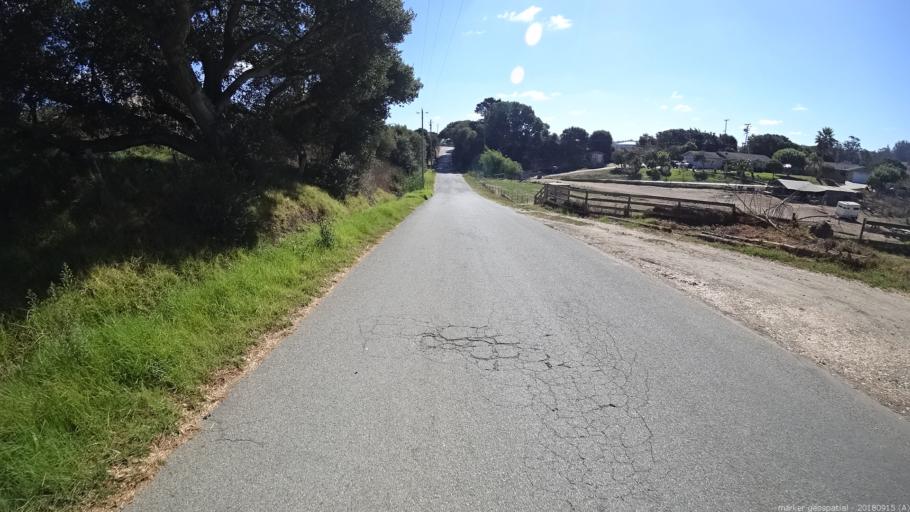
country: US
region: California
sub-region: Monterey County
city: Las Lomas
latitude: 36.8667
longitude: -121.7249
